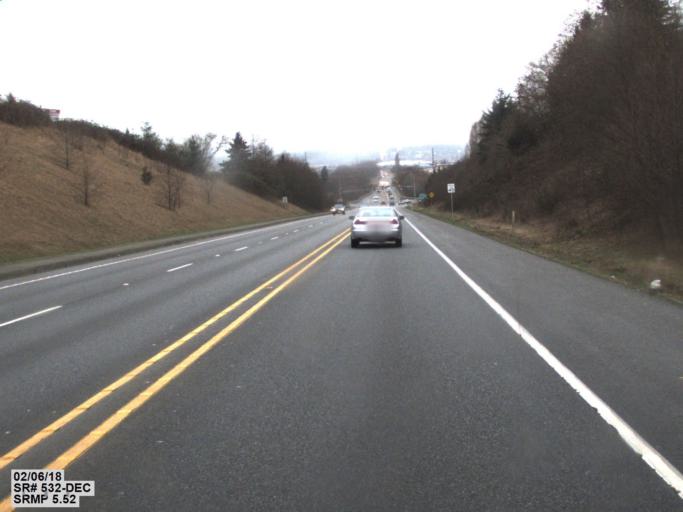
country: US
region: Washington
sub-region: Snohomish County
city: Stanwood
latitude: 48.2399
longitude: -122.3385
